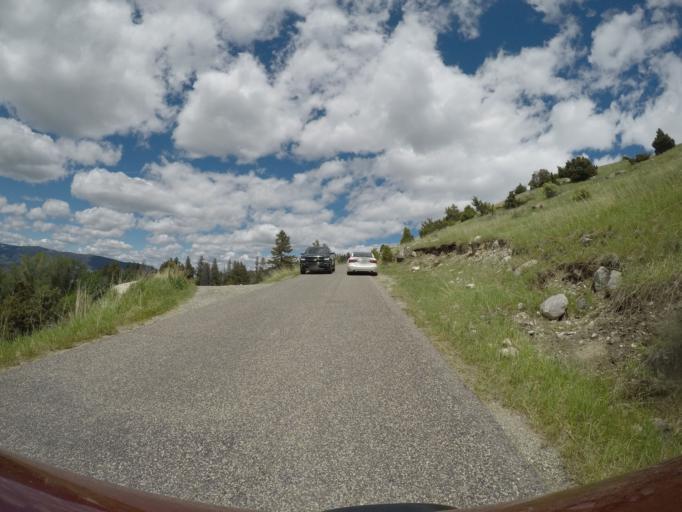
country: US
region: Montana
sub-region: Park County
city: Livingston
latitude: 45.4991
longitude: -110.5590
